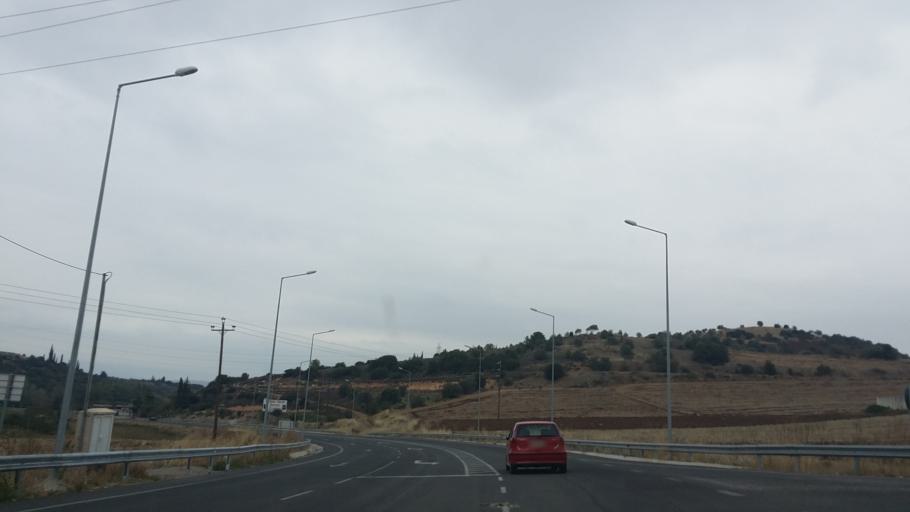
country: GR
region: Central Greece
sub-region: Nomos Voiotias
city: Thivai
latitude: 38.3095
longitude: 23.2597
